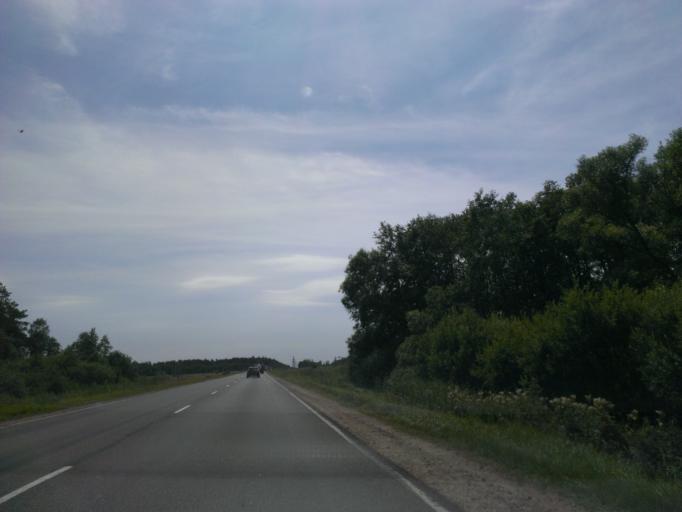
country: LV
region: Salaspils
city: Salaspils
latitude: 56.8863
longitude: 24.4074
